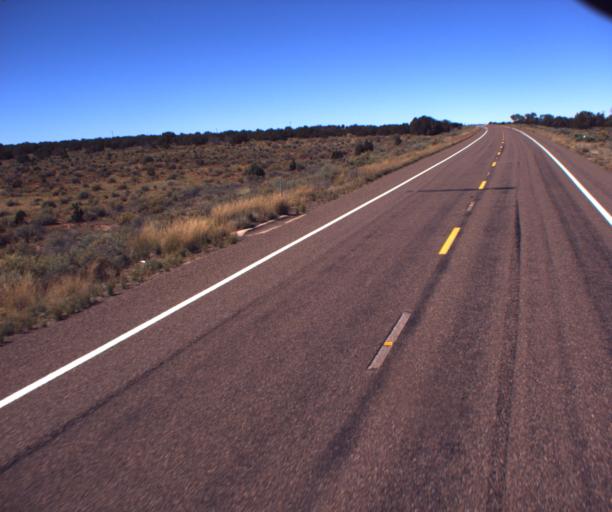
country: US
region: Arizona
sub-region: Apache County
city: Saint Johns
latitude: 34.6140
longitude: -109.6535
